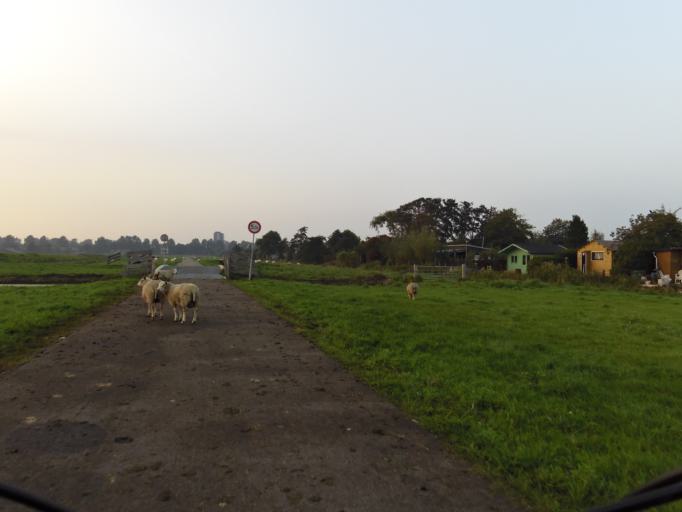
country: NL
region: South Holland
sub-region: Gemeente Leiden
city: Leiden
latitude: 52.1302
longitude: 4.4803
